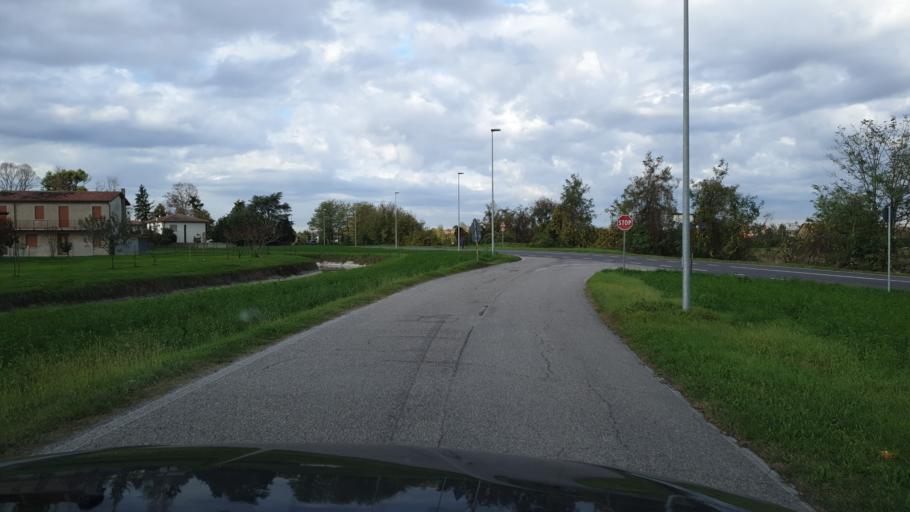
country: IT
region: Veneto
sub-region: Provincia di Rovigo
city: Villanova del Ghebbo Canton
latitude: 45.0466
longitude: 11.6470
